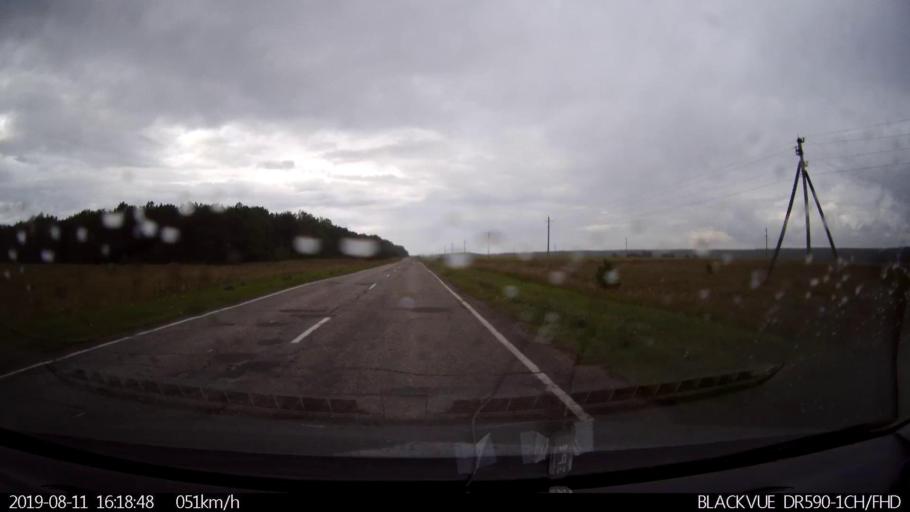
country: RU
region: Ulyanovsk
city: Mayna
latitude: 54.0576
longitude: 47.6110
